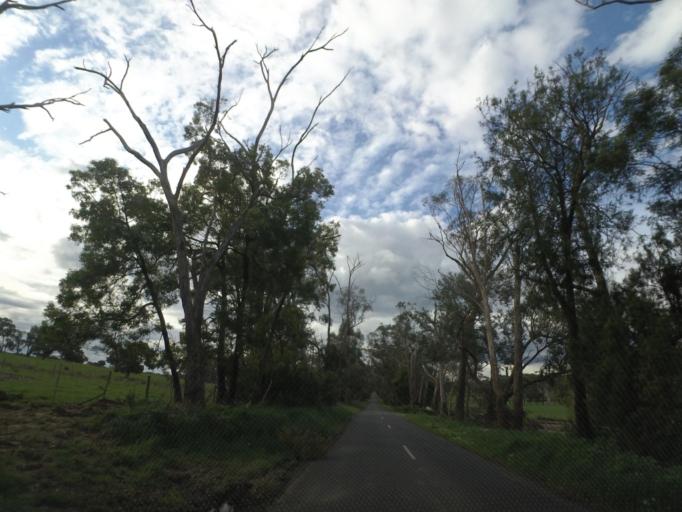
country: AU
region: Victoria
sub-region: Yarra Ranges
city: Mount Evelyn
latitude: -37.7443
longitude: 145.4123
